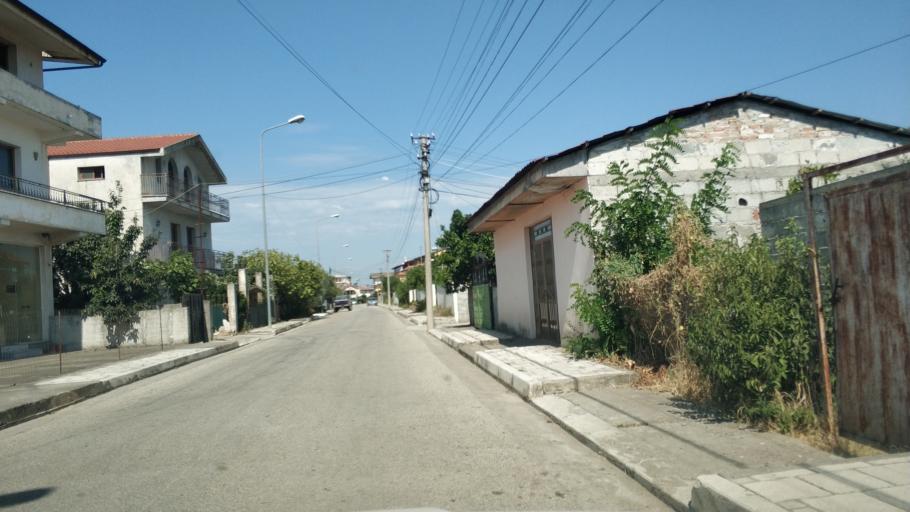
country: AL
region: Fier
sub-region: Rrethi i Lushnjes
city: Divjake
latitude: 40.9966
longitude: 19.5282
